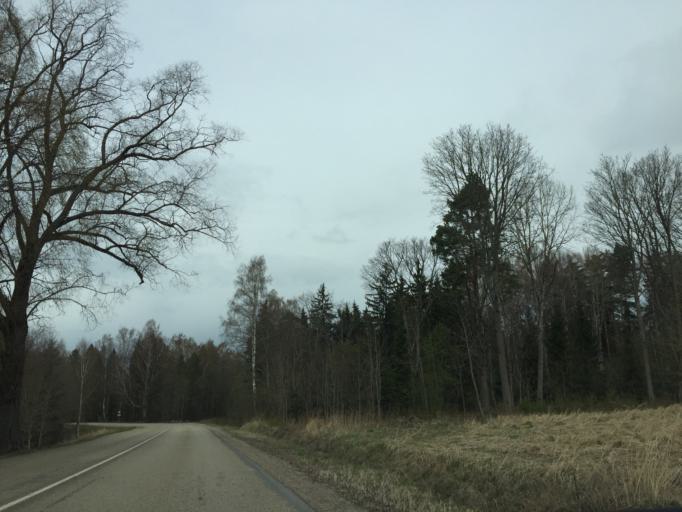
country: LV
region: Amatas Novads
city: Drabesi
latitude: 57.2593
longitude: 25.2727
